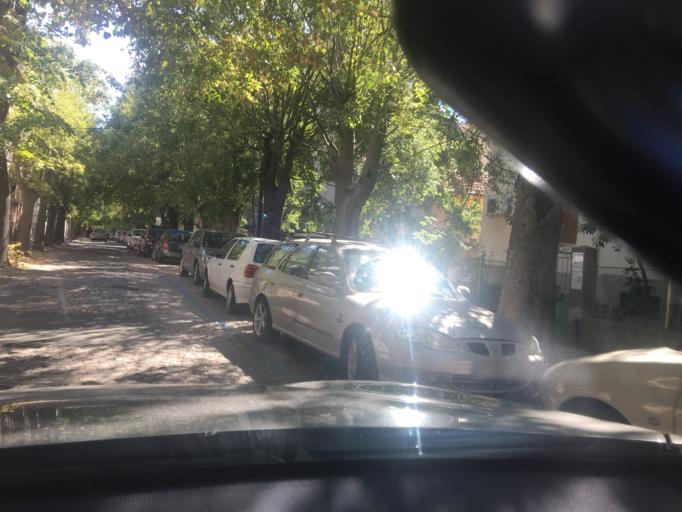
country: BG
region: Burgas
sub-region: Obshtina Burgas
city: Burgas
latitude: 42.4998
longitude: 27.4766
